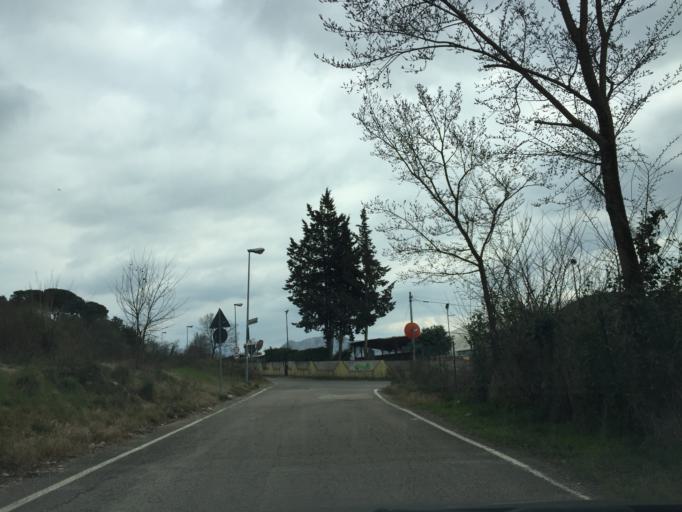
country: IT
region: Latium
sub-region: Provincia di Frosinone
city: Cassino
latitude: 41.4816
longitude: 13.8058
